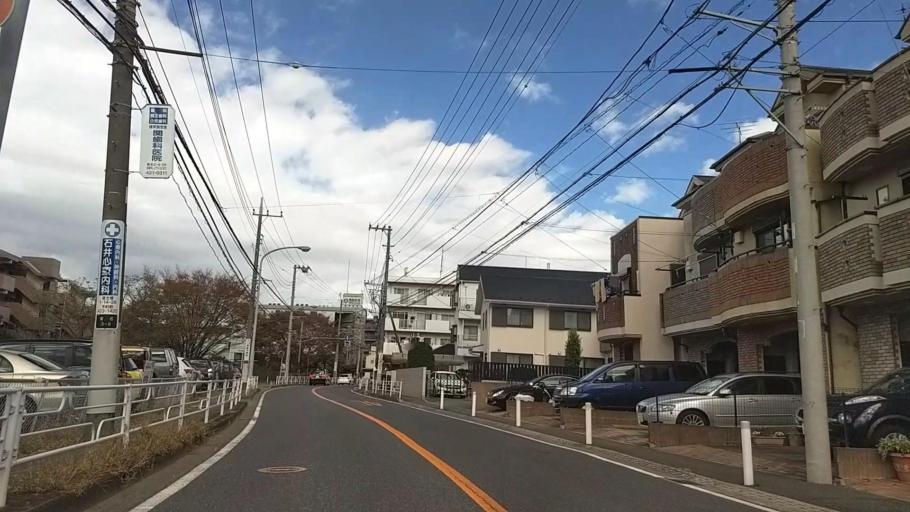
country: JP
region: Kanagawa
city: Yokohama
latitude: 35.5045
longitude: 139.6385
